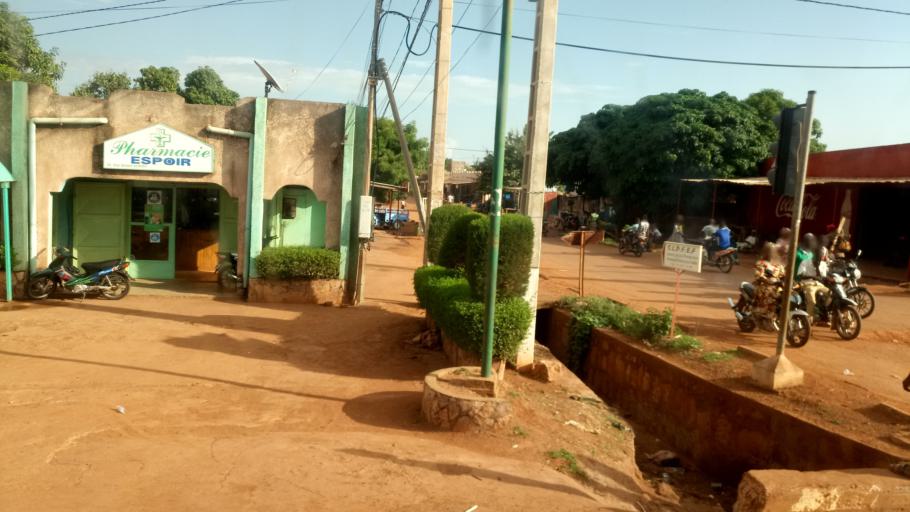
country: ML
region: Sikasso
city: Sikasso
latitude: 11.3121
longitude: -5.7001
